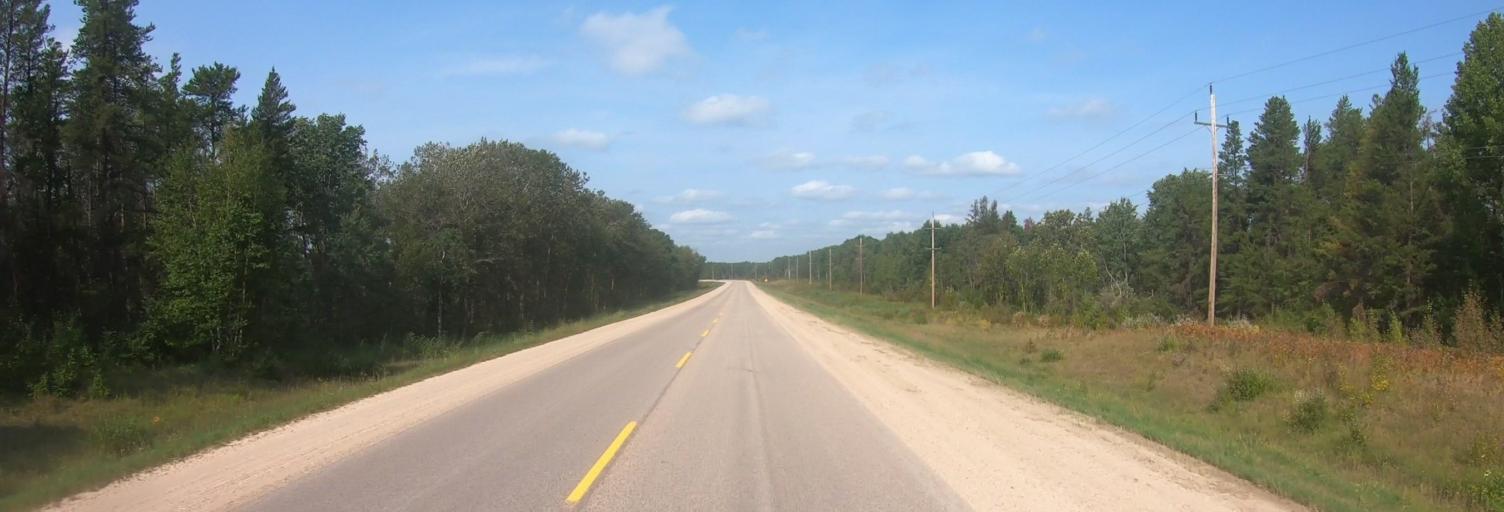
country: CA
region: Manitoba
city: La Broquerie
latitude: 49.1802
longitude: -96.1972
